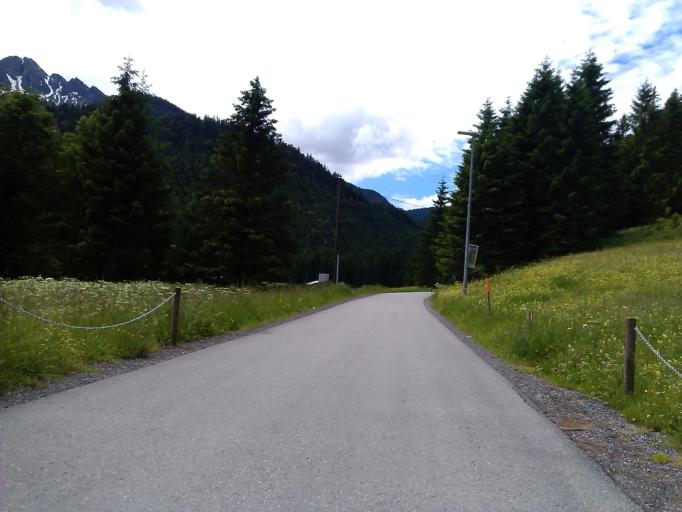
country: AT
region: Tyrol
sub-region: Politischer Bezirk Reutte
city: Ehenbichl
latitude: 47.4633
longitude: 10.7175
